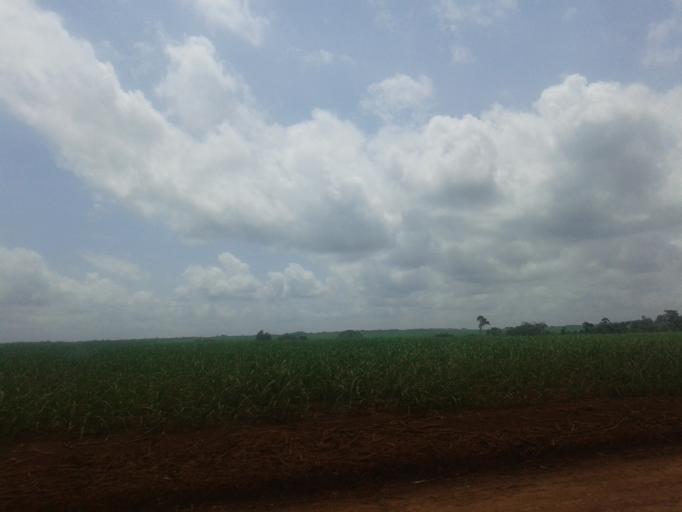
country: CM
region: Centre
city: Mbandjok
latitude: 4.4458
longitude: 11.9454
